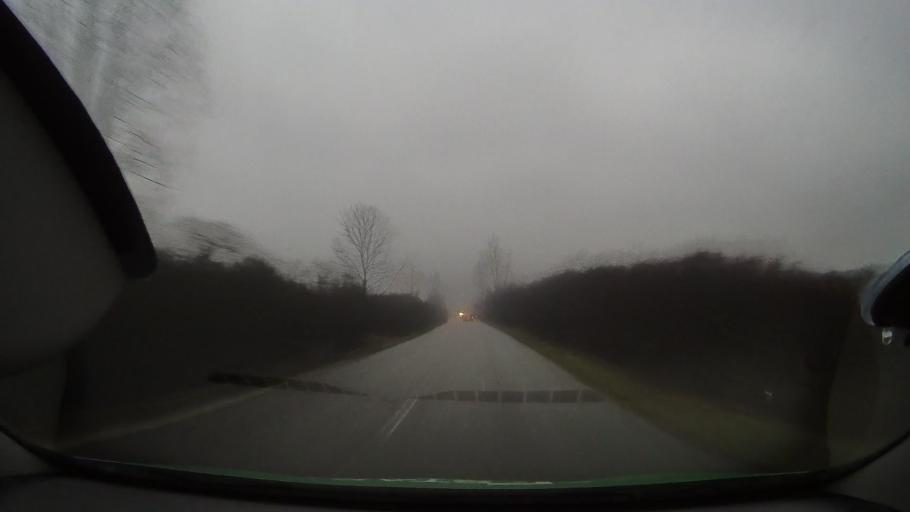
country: RO
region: Arad
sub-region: Comuna Craiova
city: Craiova
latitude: 46.5983
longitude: 21.9729
